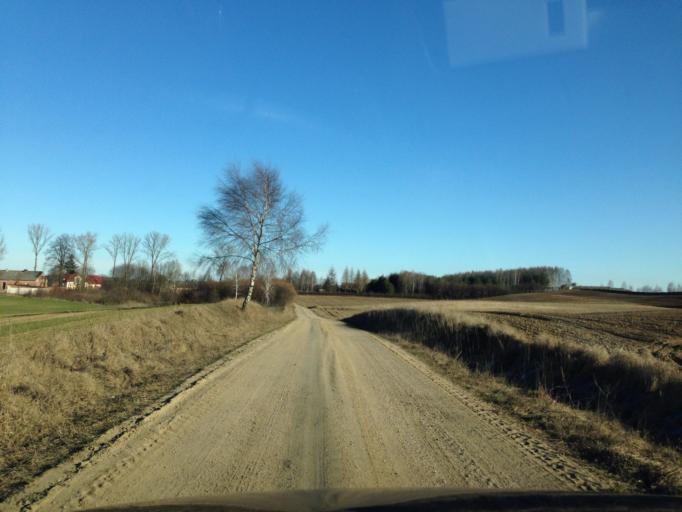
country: PL
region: Kujawsko-Pomorskie
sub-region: Powiat brodnicki
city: Brzozie
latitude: 53.3260
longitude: 19.6590
